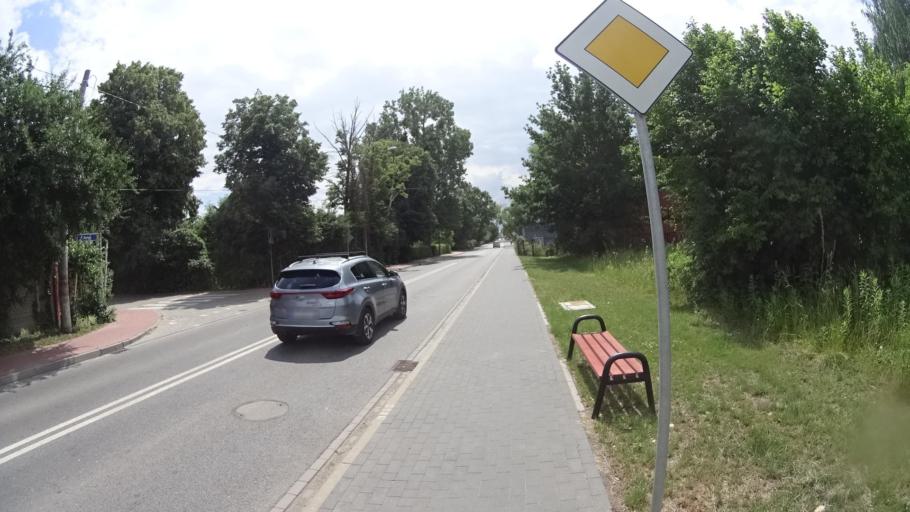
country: PL
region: Masovian Voivodeship
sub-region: Powiat pruszkowski
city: Pruszkow
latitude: 52.1686
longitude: 20.7764
